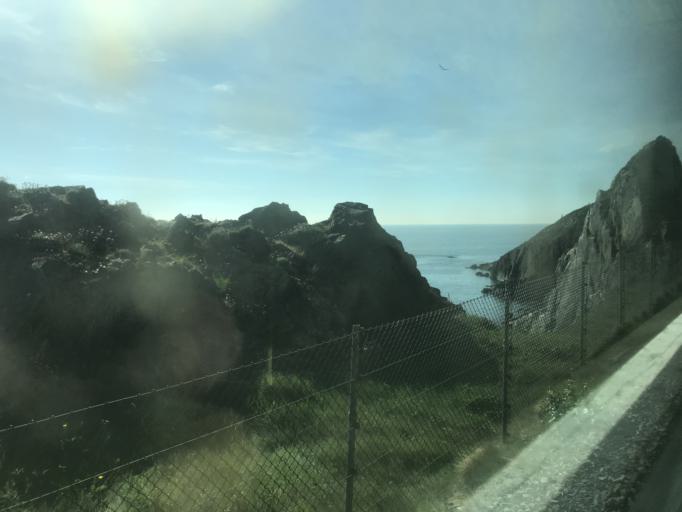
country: IE
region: Leinster
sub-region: Wicklow
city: Bray
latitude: 53.1785
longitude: -6.0751
